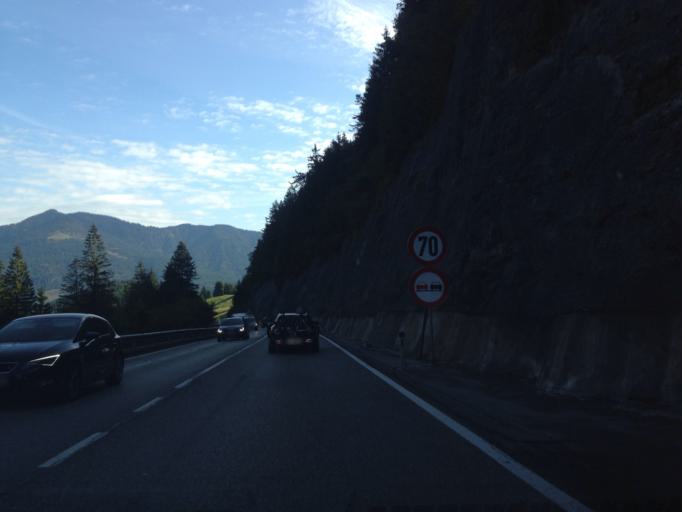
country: AT
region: Tyrol
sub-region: Politischer Bezirk Reutte
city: Reutte
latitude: 47.4649
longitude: 10.7215
